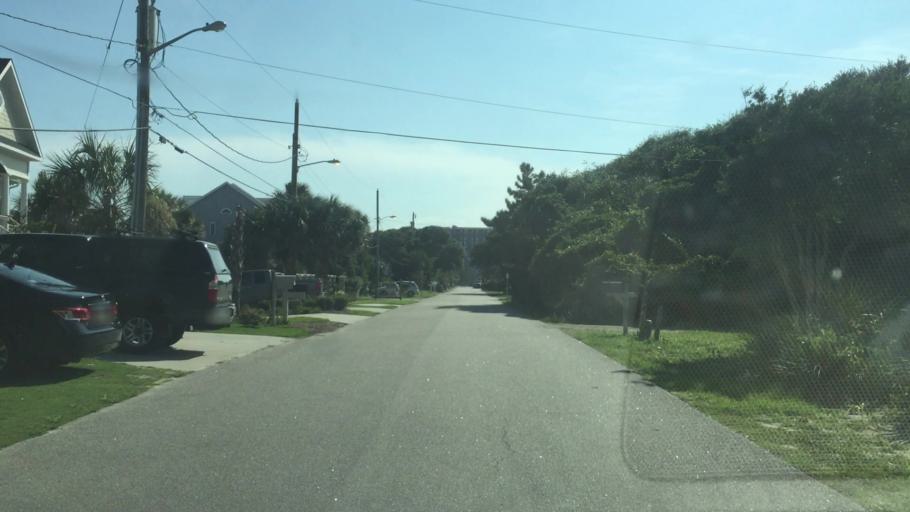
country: US
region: South Carolina
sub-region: Horry County
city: Myrtle Beach
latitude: 33.7471
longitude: -78.8090
